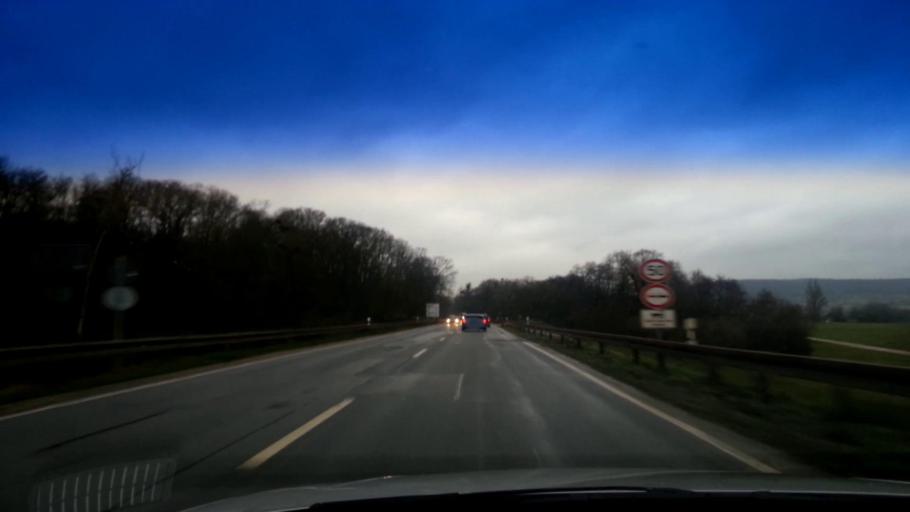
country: DE
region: Bavaria
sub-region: Upper Franconia
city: Baunach
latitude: 49.9795
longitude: 10.8587
